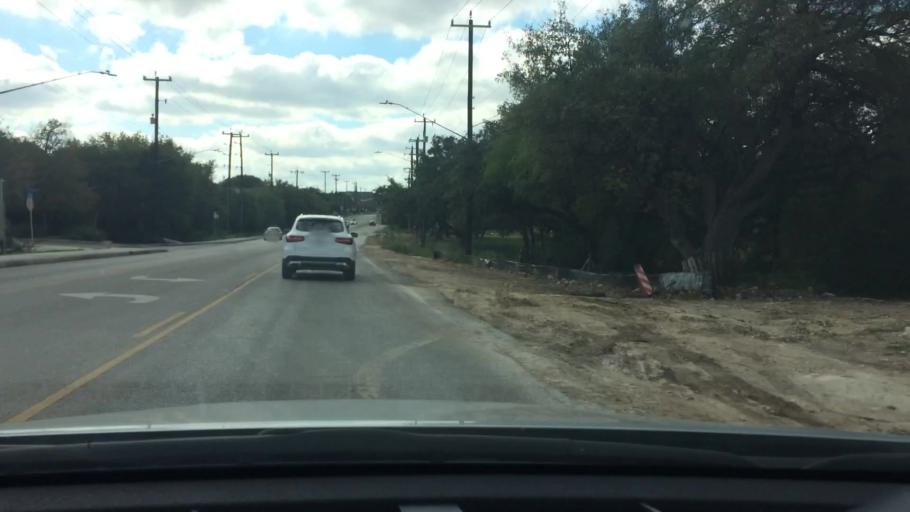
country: US
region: Texas
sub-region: Bexar County
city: Shavano Park
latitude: 29.5695
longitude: -98.5759
